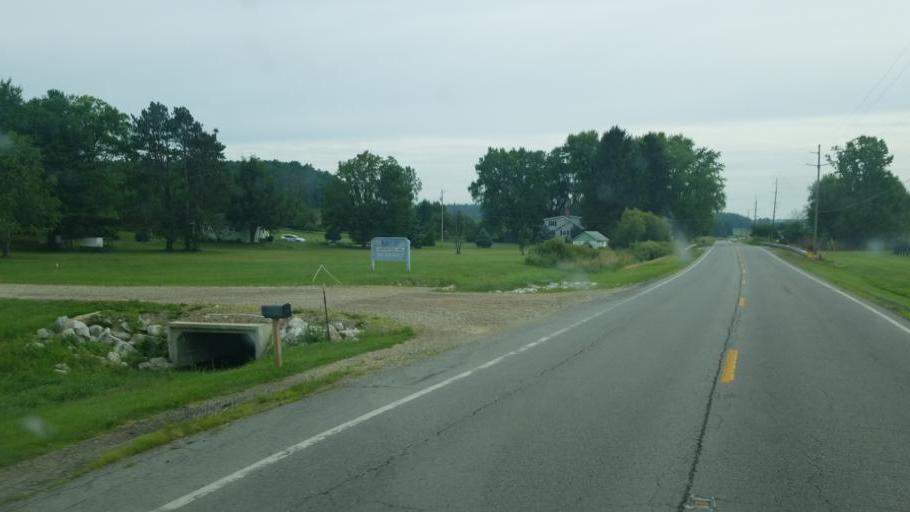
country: US
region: Ohio
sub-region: Sandusky County
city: Bellville
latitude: 40.5853
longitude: -82.5236
